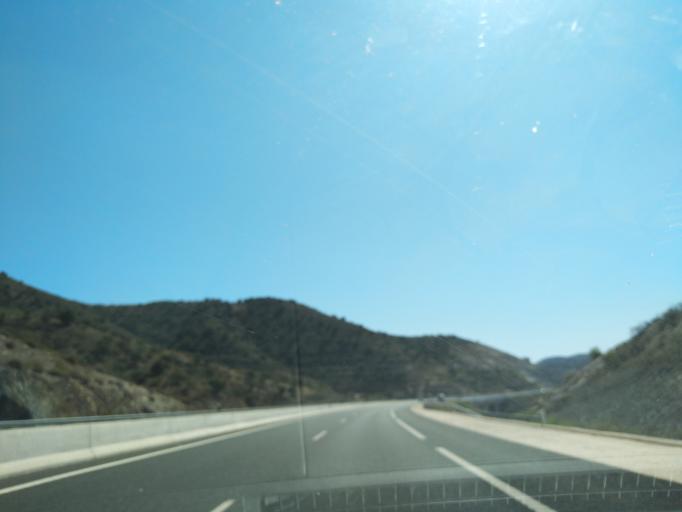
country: ES
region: Andalusia
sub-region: Provincia de Malaga
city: Almogia
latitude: 36.8334
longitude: -4.4733
